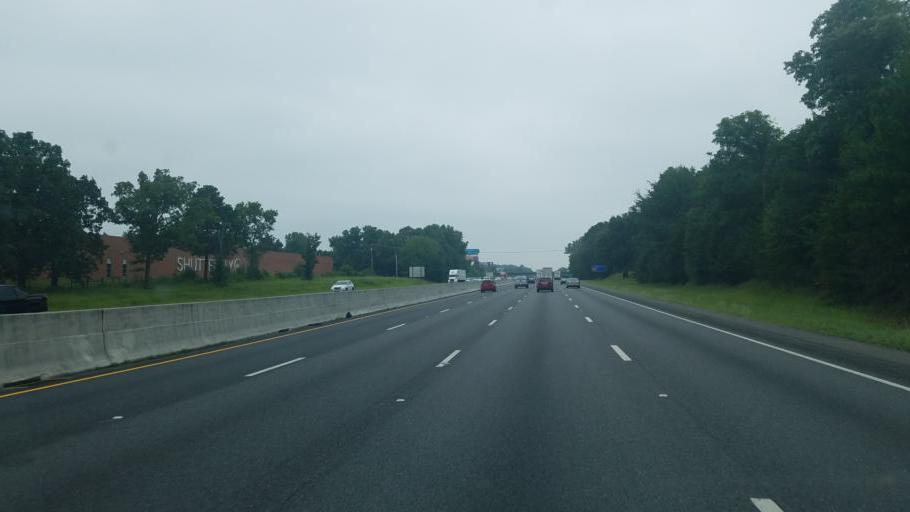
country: US
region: South Carolina
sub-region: York County
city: Fort Mill
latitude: 35.0379
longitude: -80.9602
